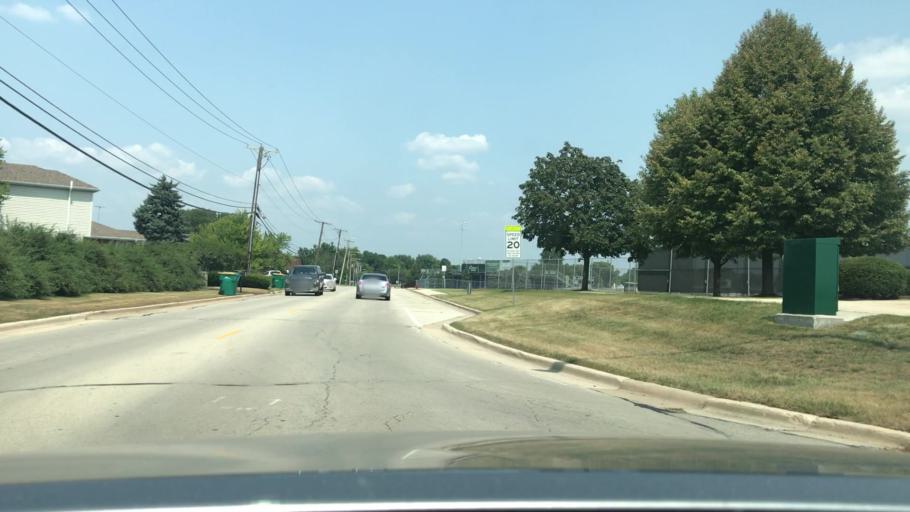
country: US
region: Illinois
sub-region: Will County
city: Plainfield
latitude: 41.6014
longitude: -88.2108
